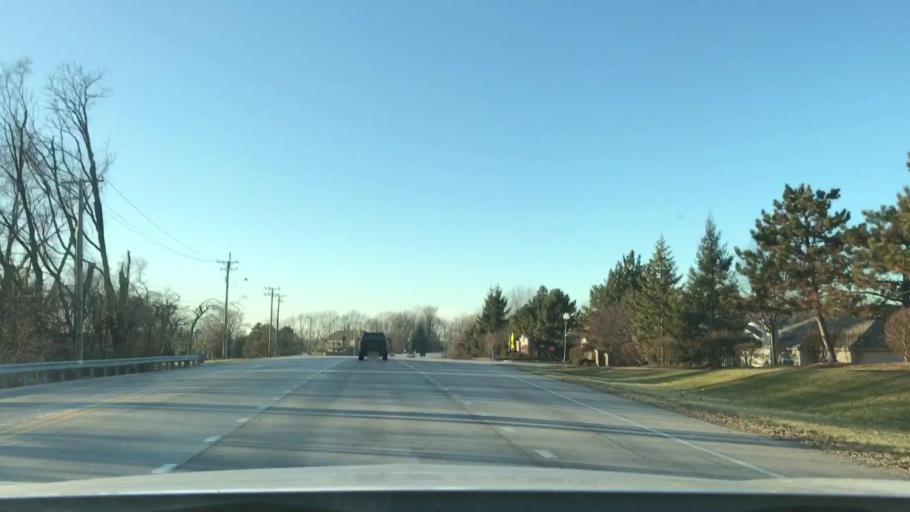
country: US
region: Illinois
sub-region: Kane County
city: Gilberts
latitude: 42.0784
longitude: -88.3770
